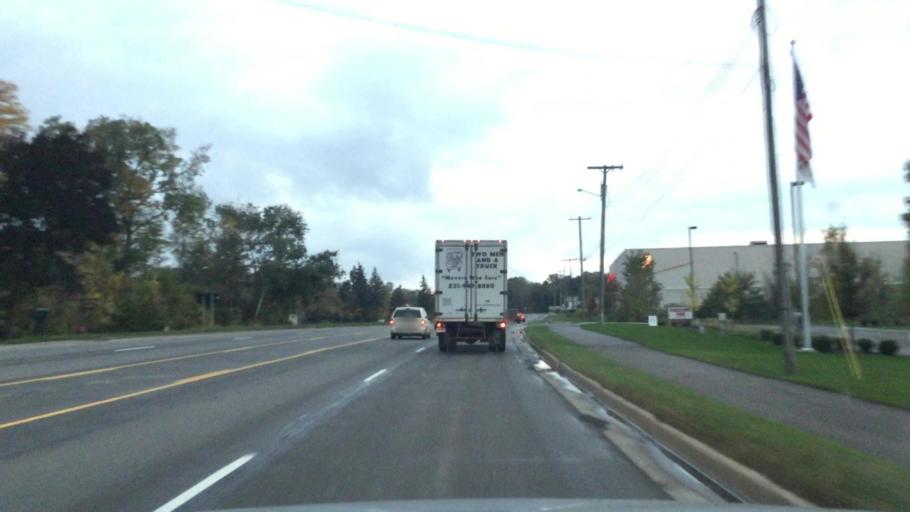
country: US
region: Michigan
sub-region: Oakland County
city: Waterford
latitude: 42.6565
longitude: -83.4707
